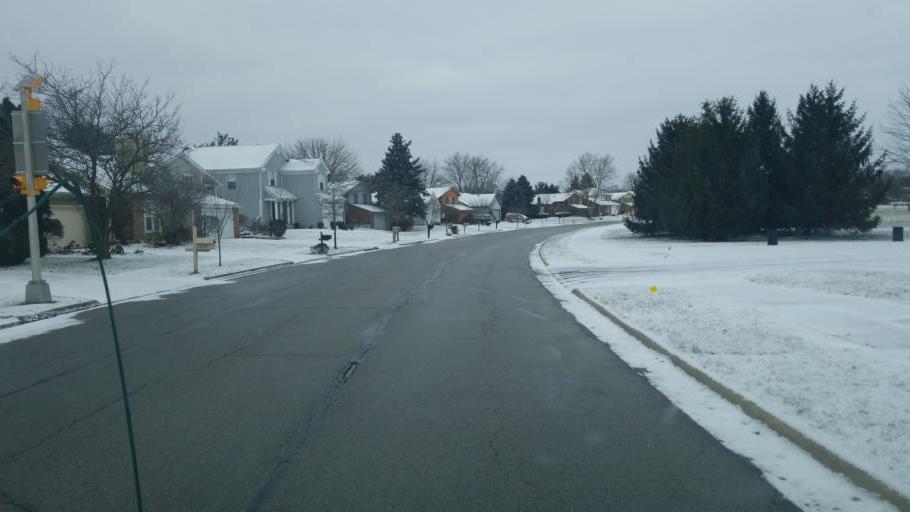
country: US
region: Ohio
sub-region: Delaware County
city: Powell
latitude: 40.1202
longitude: -83.0819
